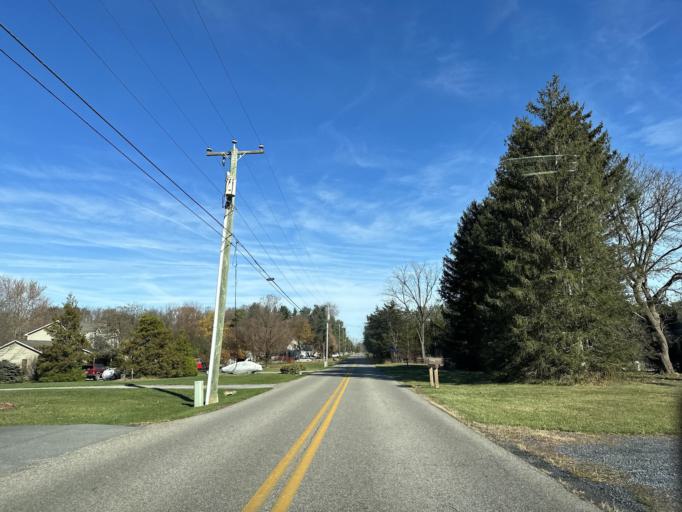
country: US
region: Virginia
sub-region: Augusta County
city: Crimora
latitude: 38.2077
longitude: -78.9029
